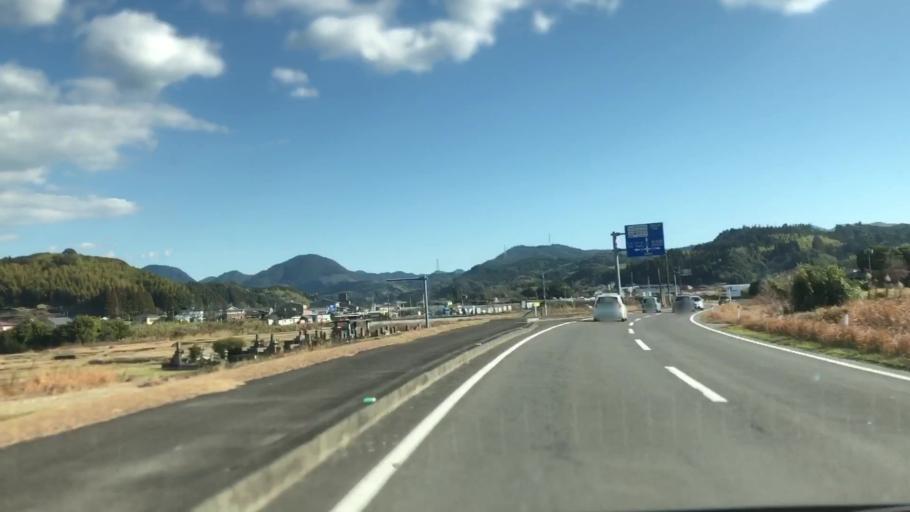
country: JP
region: Kagoshima
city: Satsumasendai
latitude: 31.7961
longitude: 130.4378
